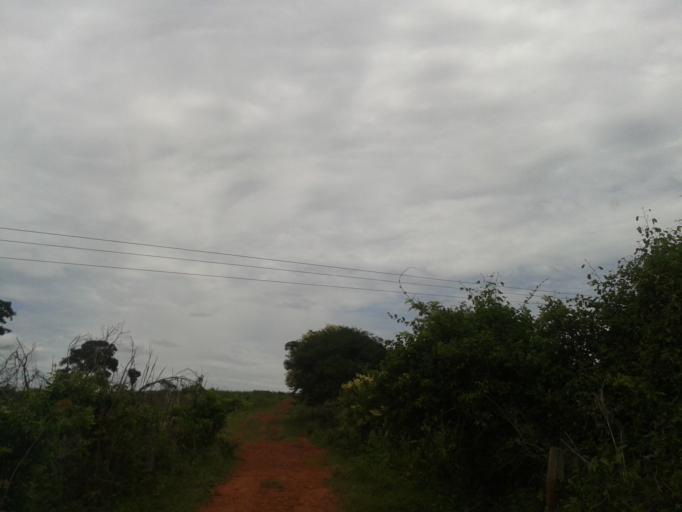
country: BR
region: Minas Gerais
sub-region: Santa Vitoria
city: Santa Vitoria
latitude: -19.2186
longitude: -50.6008
